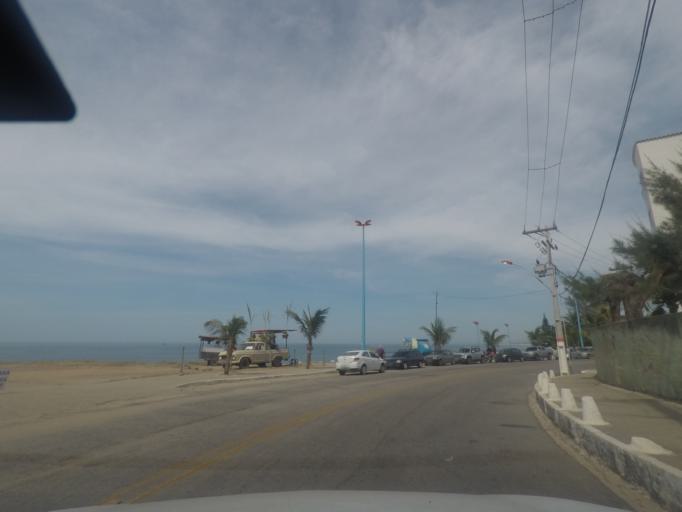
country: BR
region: Rio de Janeiro
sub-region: Marica
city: Marica
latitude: -22.9573
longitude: -42.6949
